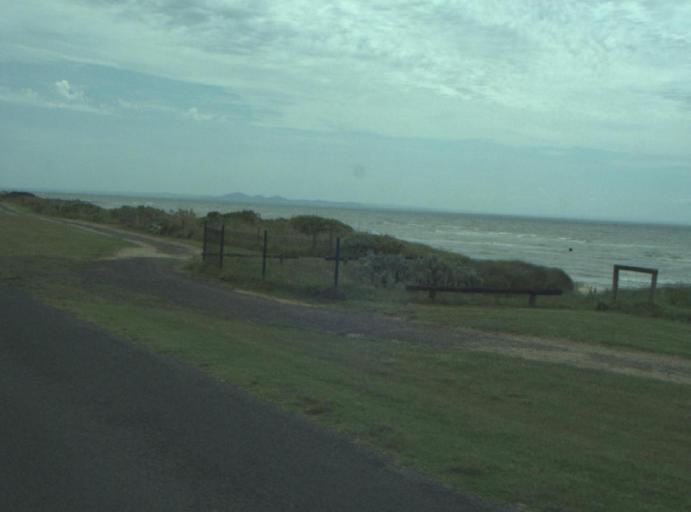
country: AU
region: Victoria
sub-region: Greater Geelong
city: Clifton Springs
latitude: -38.1174
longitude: 144.6829
